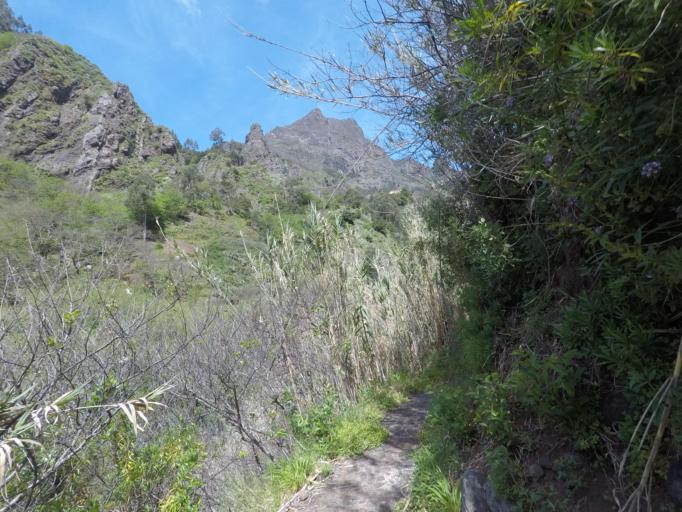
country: PT
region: Madeira
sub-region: Camara de Lobos
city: Curral das Freiras
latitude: 32.7294
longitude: -16.9677
